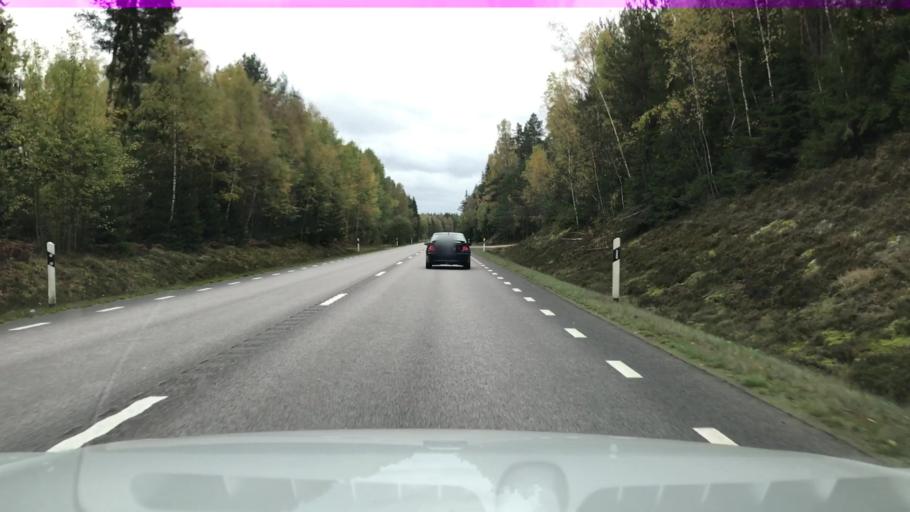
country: SE
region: Kalmar
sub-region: Hultsfreds Kommun
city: Hultsfred
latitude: 57.5466
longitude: 15.8457
